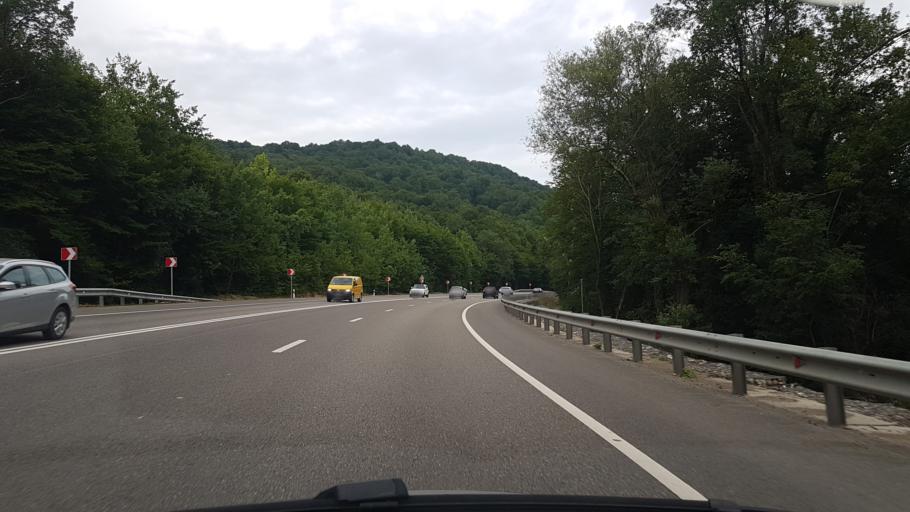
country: RU
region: Krasnodarskiy
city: Dzhubga
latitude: 44.4001
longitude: 38.7380
